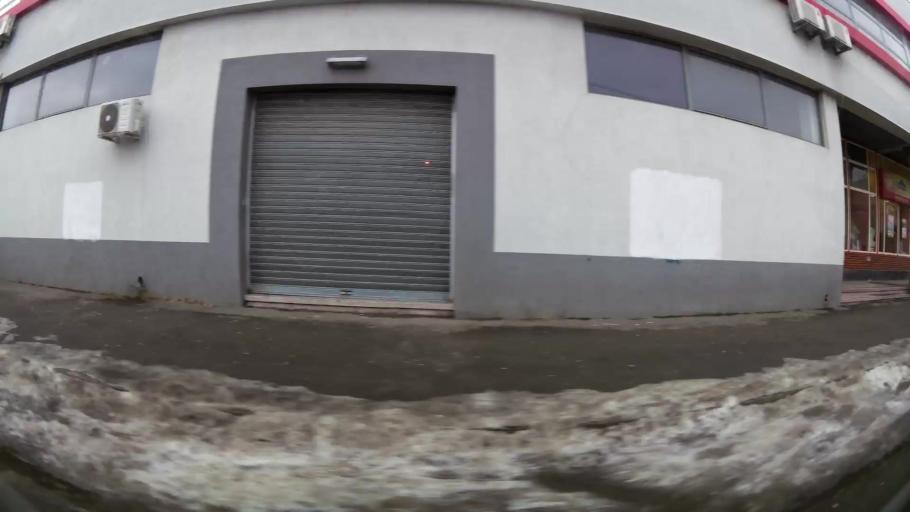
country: RO
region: Ilfov
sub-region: Comuna Pantelimon
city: Pantelimon
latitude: 44.4332
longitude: 26.2006
